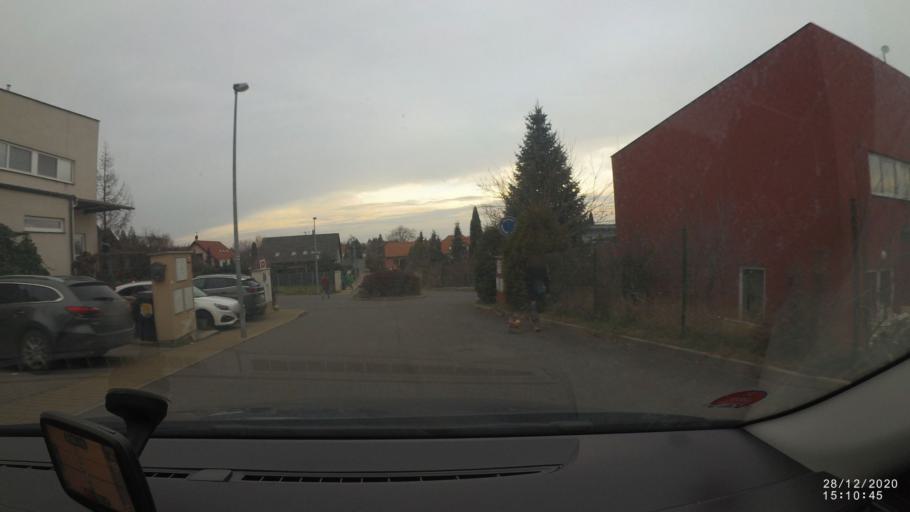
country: CZ
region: Central Bohemia
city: Uvaly
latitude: 50.0653
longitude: 14.7324
